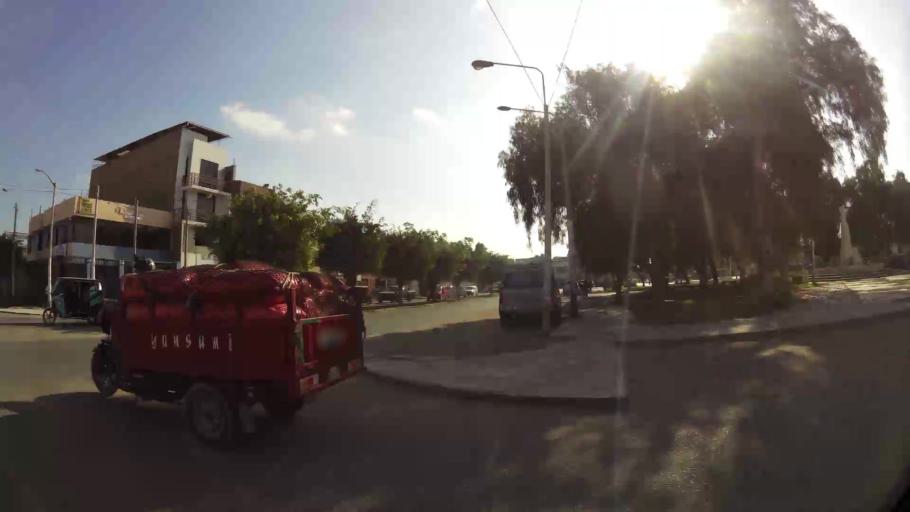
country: PE
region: Lambayeque
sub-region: Provincia de Chiclayo
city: Chiclayo
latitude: -6.7656
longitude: -79.8518
